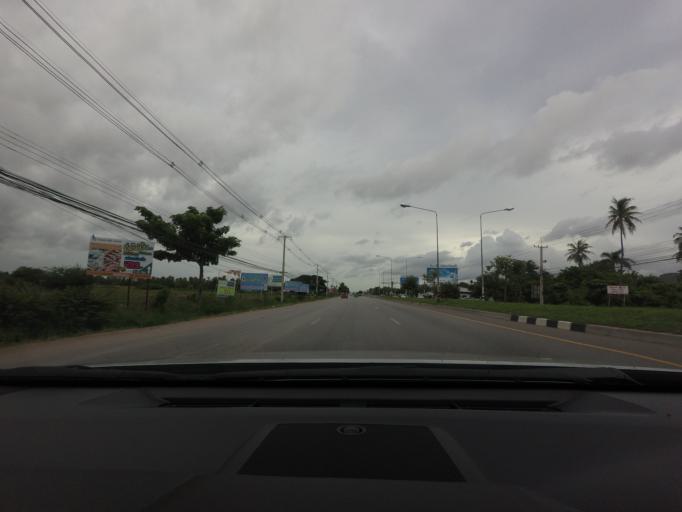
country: TH
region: Phetchaburi
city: Cha-am
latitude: 12.8457
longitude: 99.9281
